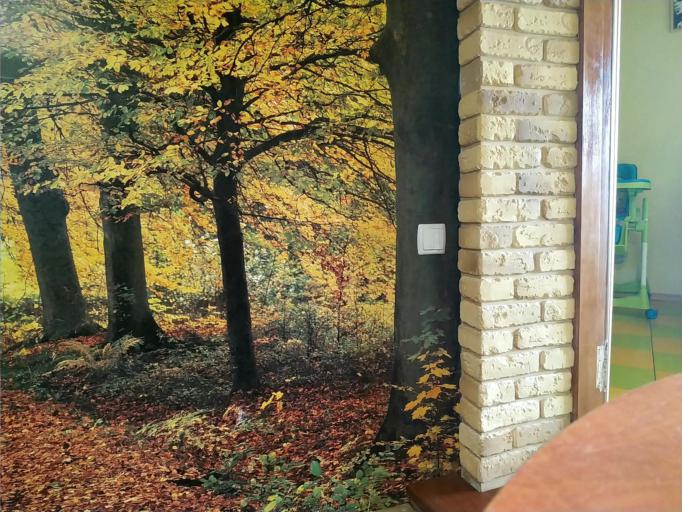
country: RU
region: Smolensk
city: Ozernyy
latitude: 55.4700
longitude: 32.6643
